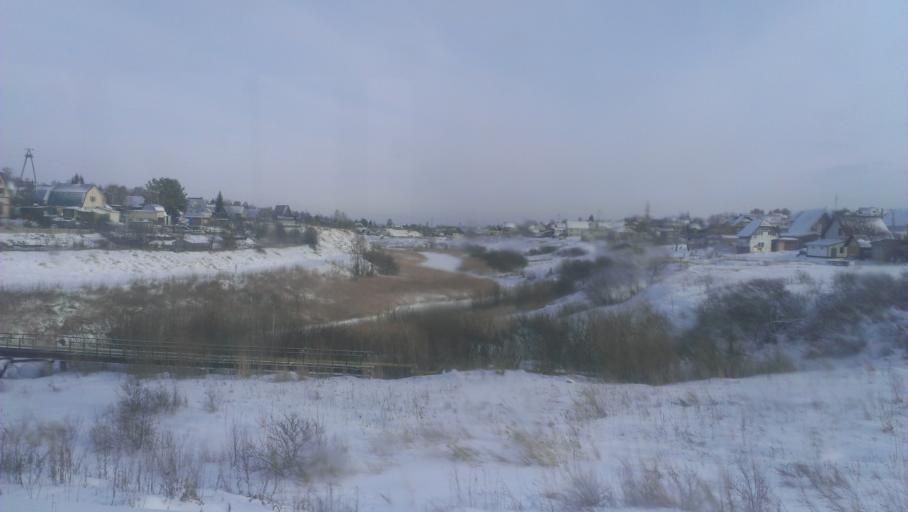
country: RU
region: Altai Krai
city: Gon'ba
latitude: 53.4150
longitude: 83.5507
